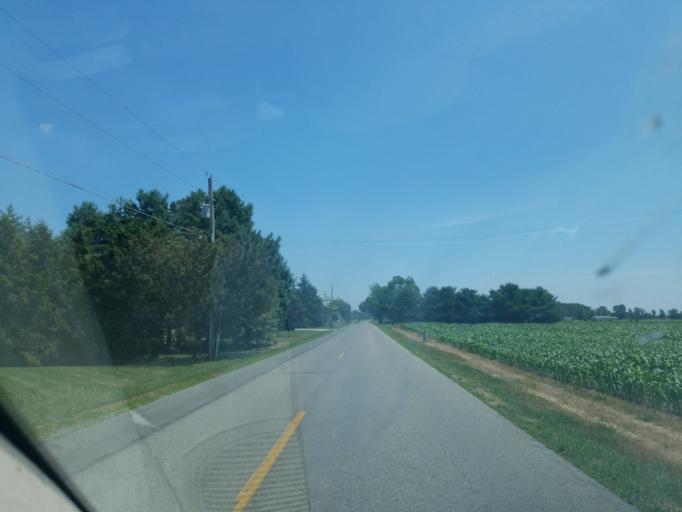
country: US
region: Ohio
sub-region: Allen County
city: Elida
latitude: 40.7874
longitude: -84.2493
